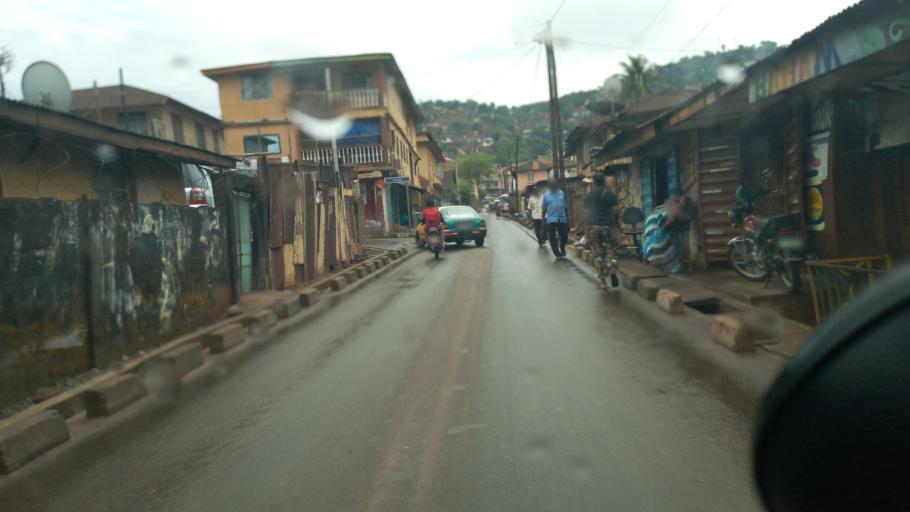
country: SL
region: Western Area
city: Freetown
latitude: 8.4770
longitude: -13.2345
